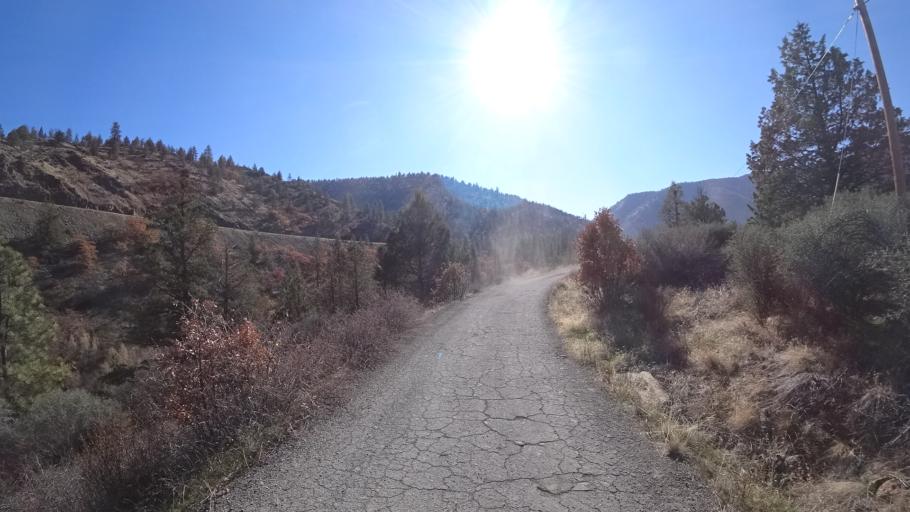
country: US
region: California
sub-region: Siskiyou County
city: Yreka
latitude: 41.8023
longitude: -122.6012
